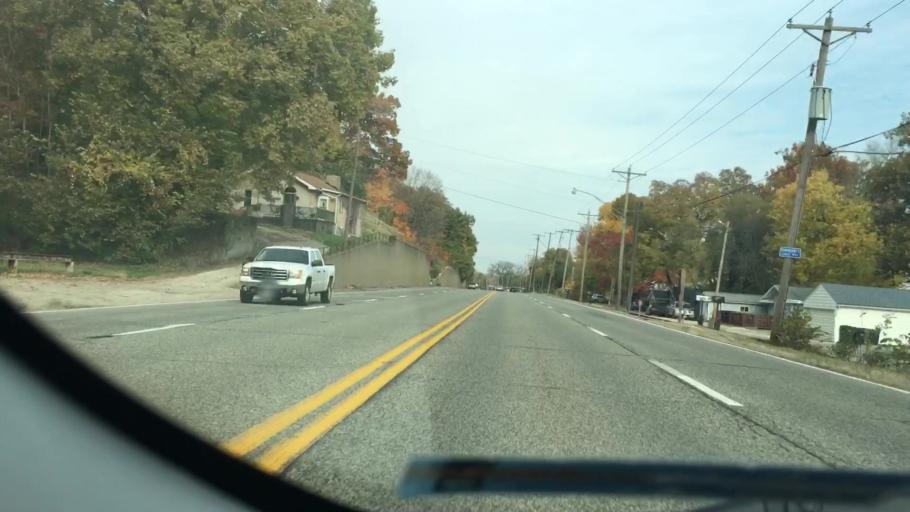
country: US
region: Illinois
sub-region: Peoria County
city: Peoria Heights
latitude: 40.7378
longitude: -89.5526
